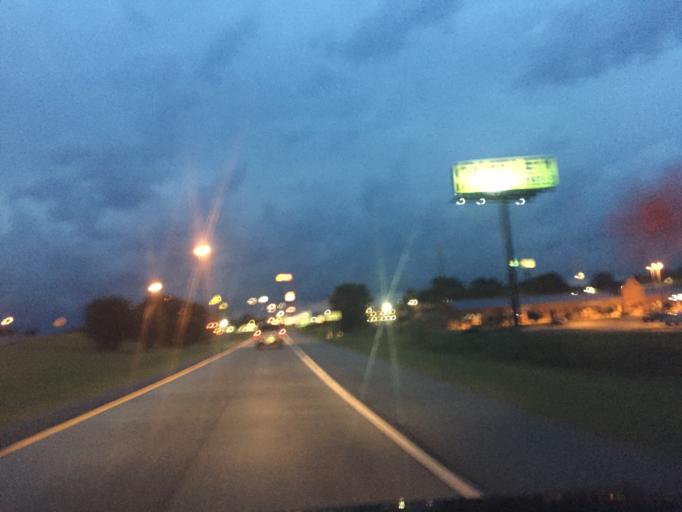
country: US
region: Georgia
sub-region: Chatham County
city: Georgetown
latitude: 32.0019
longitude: -81.2857
